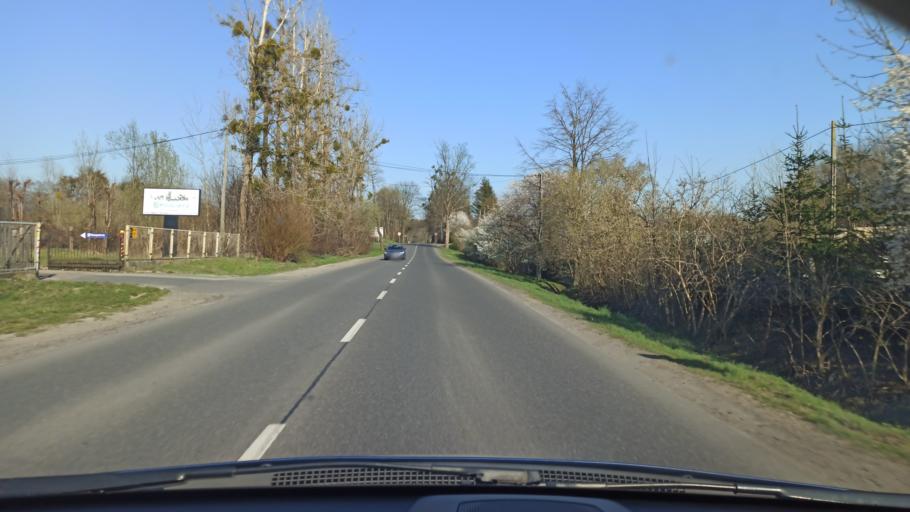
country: PL
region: Warmian-Masurian Voivodeship
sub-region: Powiat elblaski
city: Elblag
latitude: 54.1839
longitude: 19.4412
